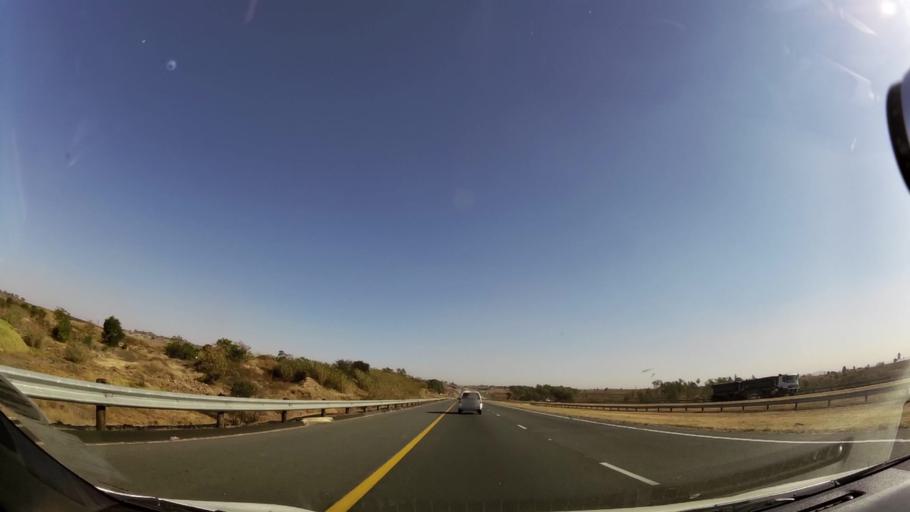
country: ZA
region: Gauteng
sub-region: City of Johannesburg Metropolitan Municipality
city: Diepsloot
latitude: -25.9764
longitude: 27.9361
